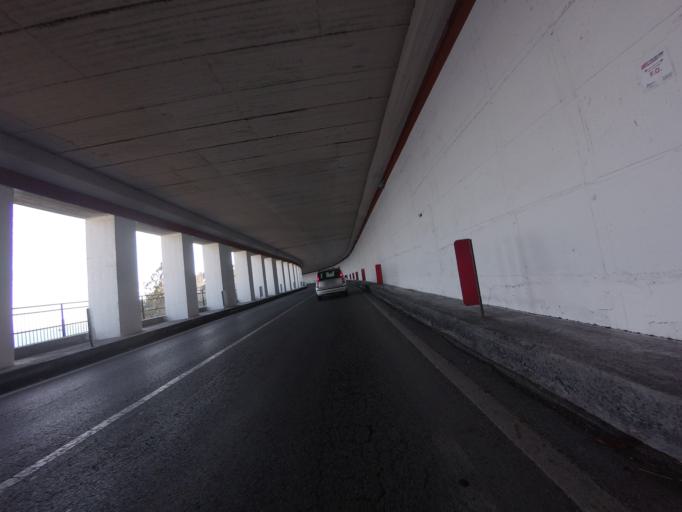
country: IT
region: Sicily
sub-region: Messina
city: Taormina
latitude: 37.8509
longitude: 15.2968
